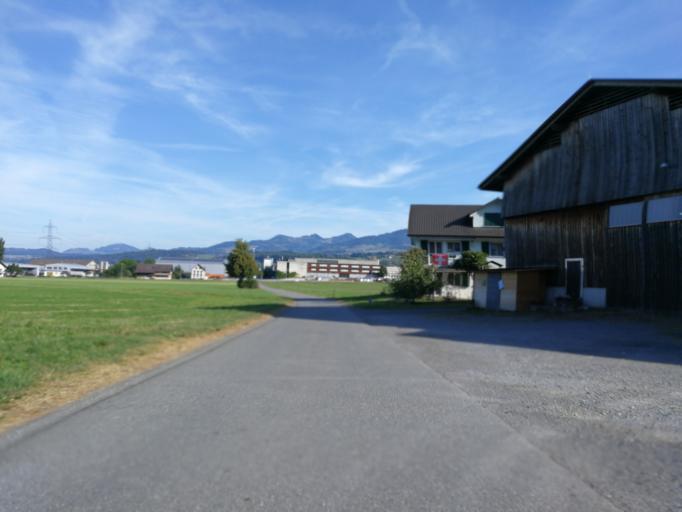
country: CH
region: Saint Gallen
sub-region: Wahlkreis See-Gaster
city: Kaltbrunn
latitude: 47.2051
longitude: 9.0234
